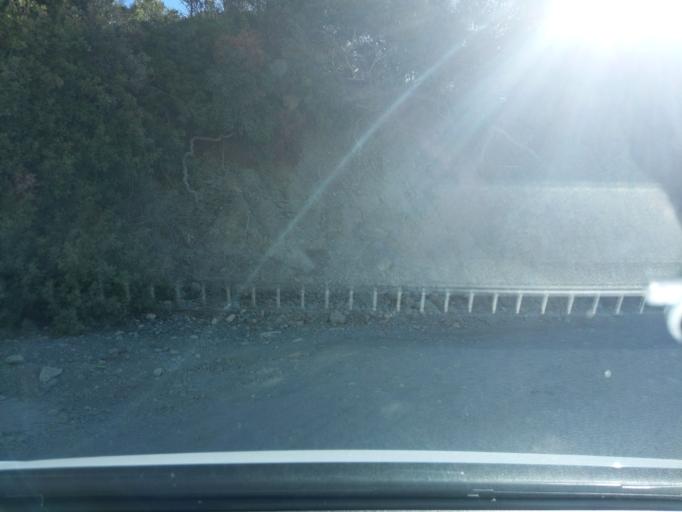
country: GR
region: Crete
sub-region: Nomos Irakleiou
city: Moires
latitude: 34.9396
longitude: 24.8131
